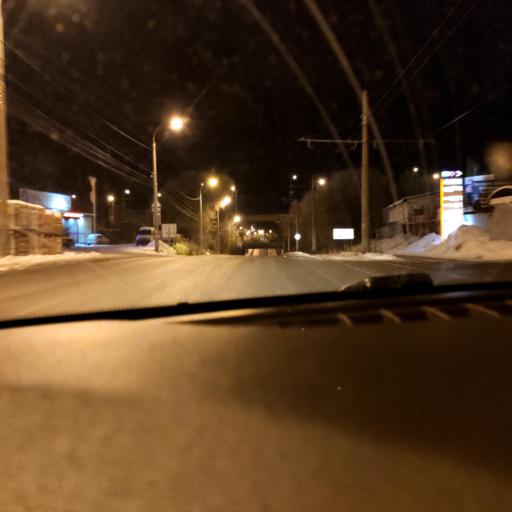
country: RU
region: Samara
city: Smyshlyayevka
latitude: 53.2238
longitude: 50.2808
